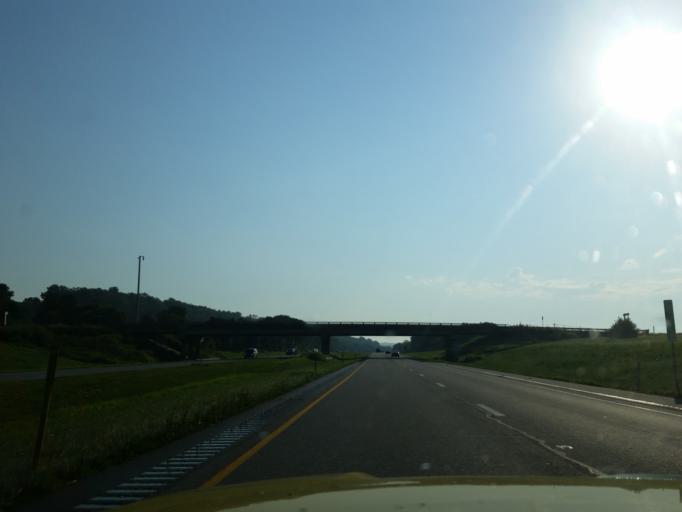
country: US
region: Pennsylvania
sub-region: York County
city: Wrightsville
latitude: 40.0274
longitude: -76.5549
